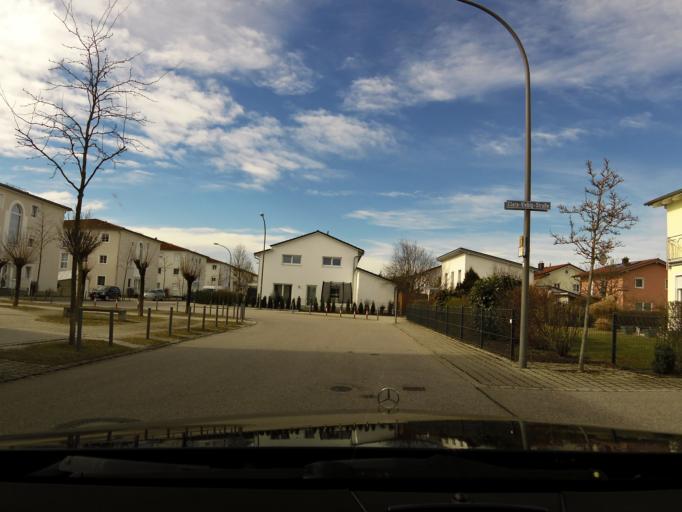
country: DE
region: Bavaria
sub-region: Lower Bavaria
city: Landshut
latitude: 48.5562
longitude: 12.1226
